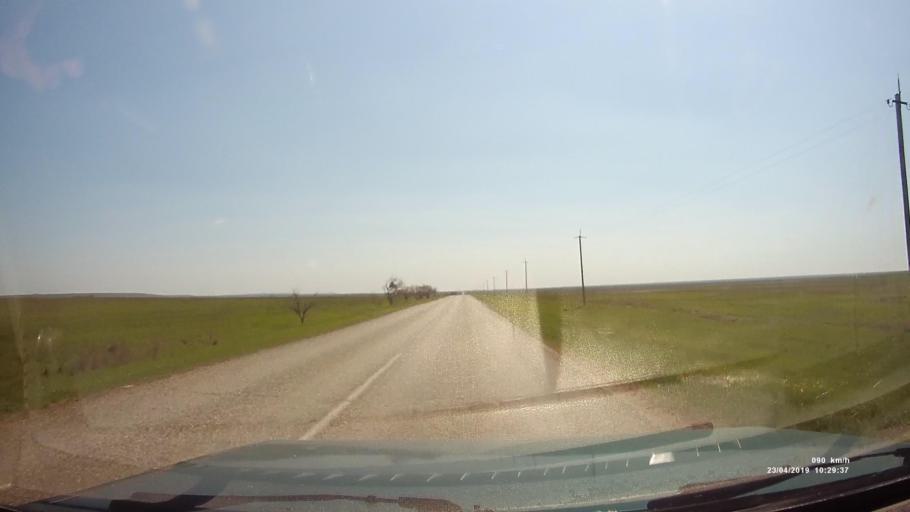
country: RU
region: Kalmykiya
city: Yashalta
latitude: 46.5974
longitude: 42.5295
